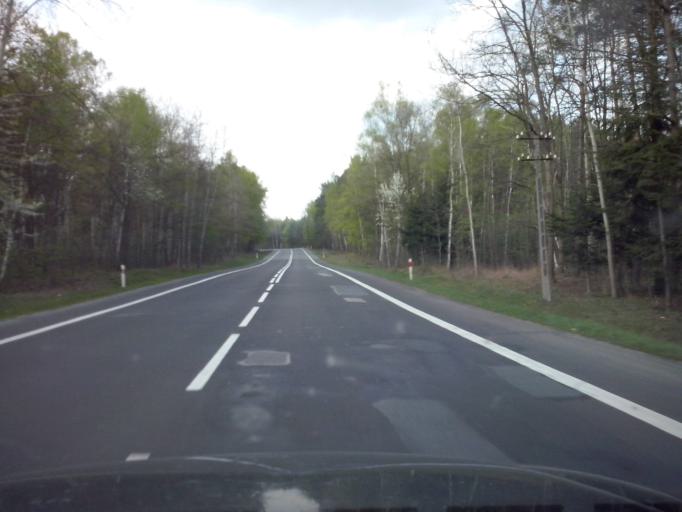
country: PL
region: Subcarpathian Voivodeship
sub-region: Powiat rzeszowski
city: Gorno
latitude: 50.2706
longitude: 22.1410
